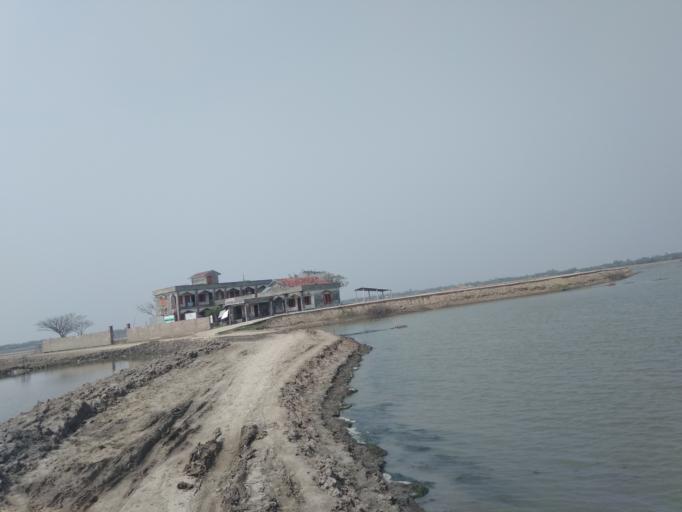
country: IN
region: West Bengal
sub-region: North 24 Parganas
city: Taki
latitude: 22.3450
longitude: 89.2296
